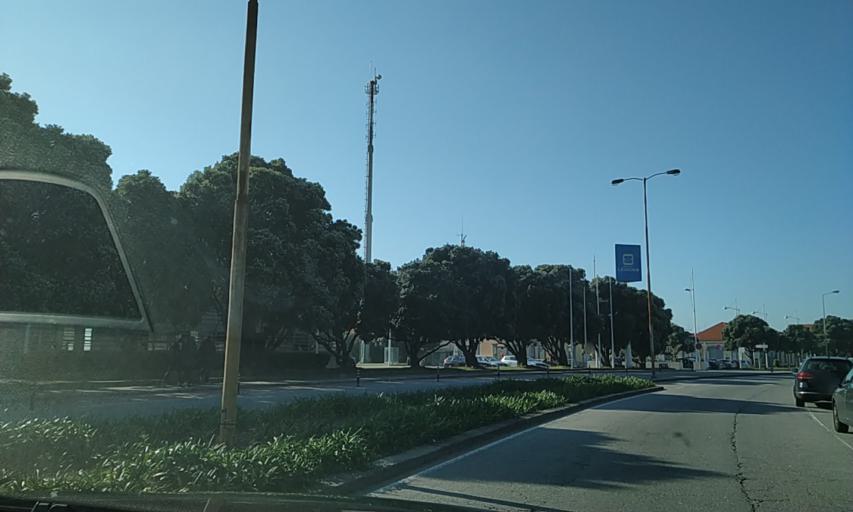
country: PT
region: Porto
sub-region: Matosinhos
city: Leca da Palmeira
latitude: 41.1870
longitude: -8.7021
